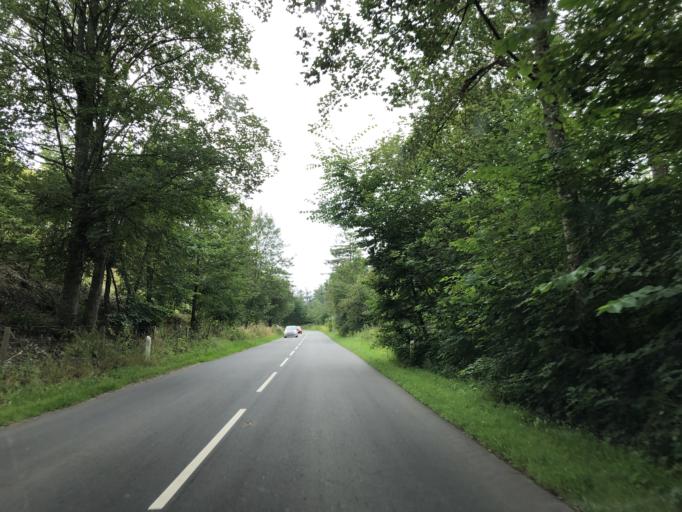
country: DK
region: Central Jutland
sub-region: Viborg Kommune
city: Stoholm
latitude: 56.4550
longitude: 9.1660
